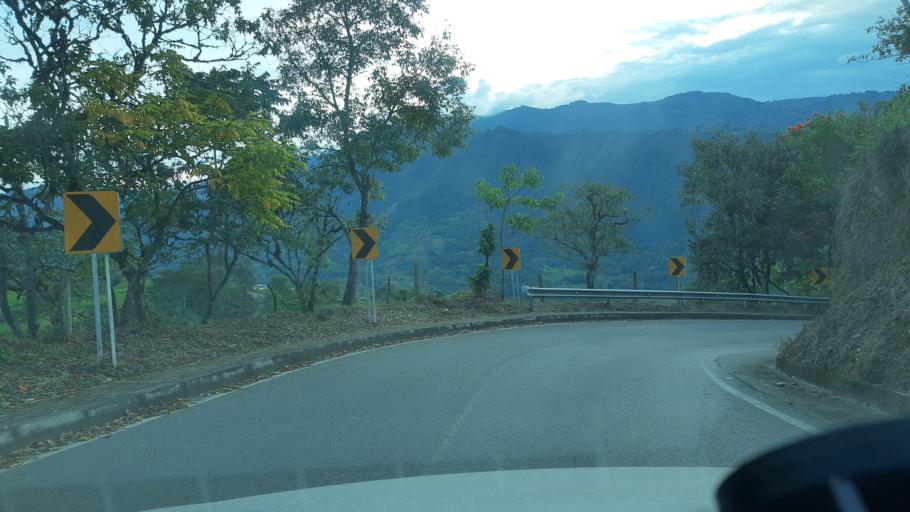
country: CO
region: Boyaca
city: Chivor
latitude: 4.9766
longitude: -73.3308
